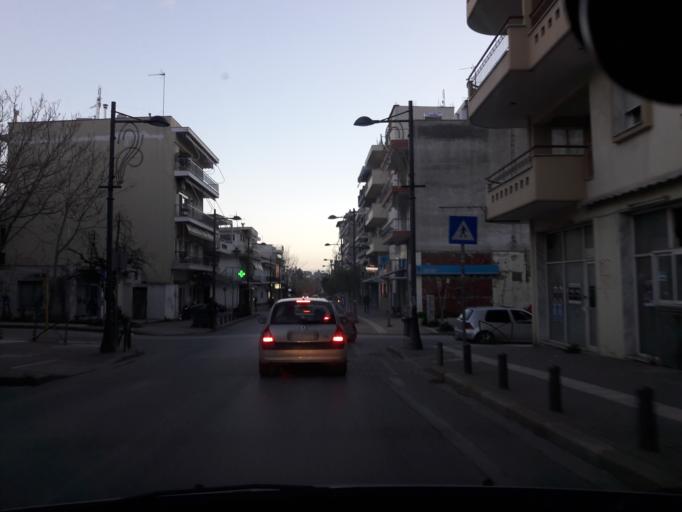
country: GR
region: Central Macedonia
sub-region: Nomos Thessalonikis
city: Stavroupoli
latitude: 40.6681
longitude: 22.9327
